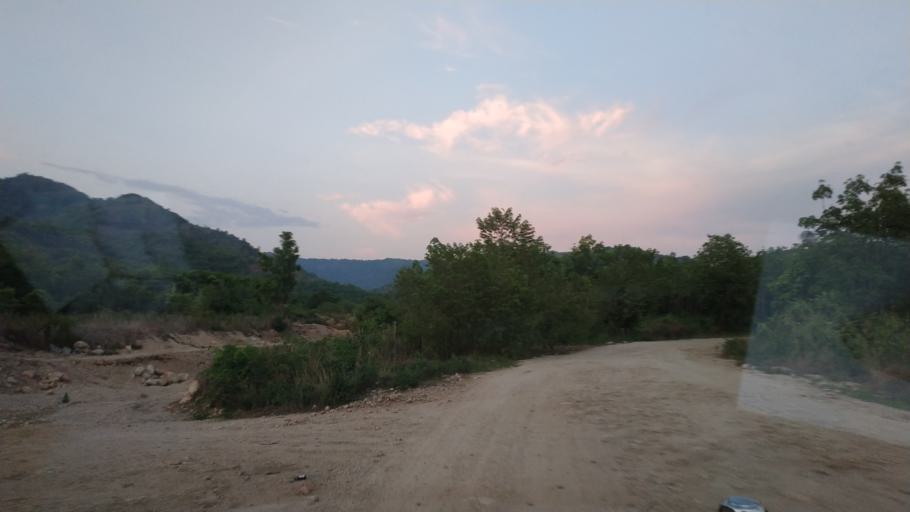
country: MM
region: Mon
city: Kyaikto
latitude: 17.4168
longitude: 97.0591
